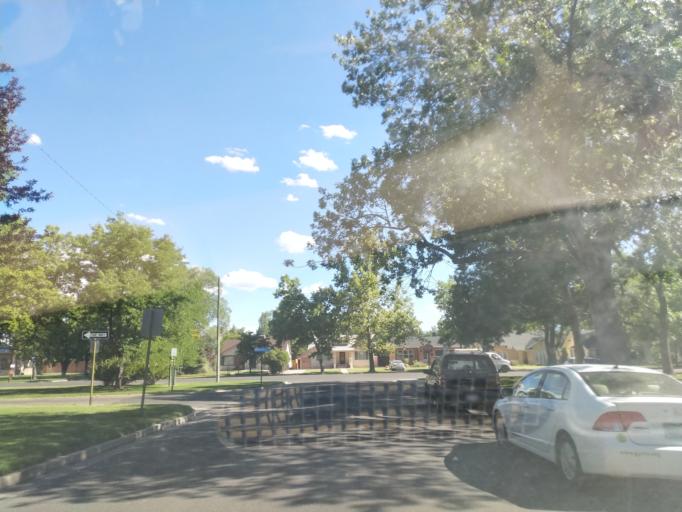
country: US
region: Colorado
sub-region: Mesa County
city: Grand Junction
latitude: 39.0739
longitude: -108.5494
